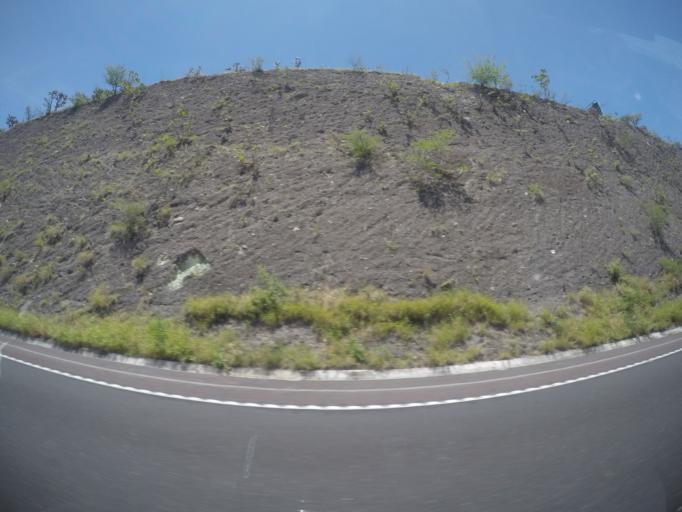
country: MX
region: Morelos
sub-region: Jojutla
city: Higueron
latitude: 18.5269
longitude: -99.1986
